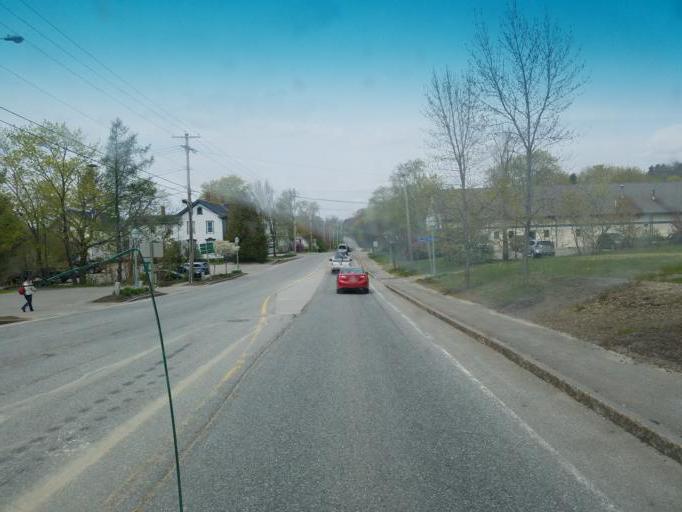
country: US
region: Maine
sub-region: Hancock County
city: Ellsworth
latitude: 44.5434
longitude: -68.4204
